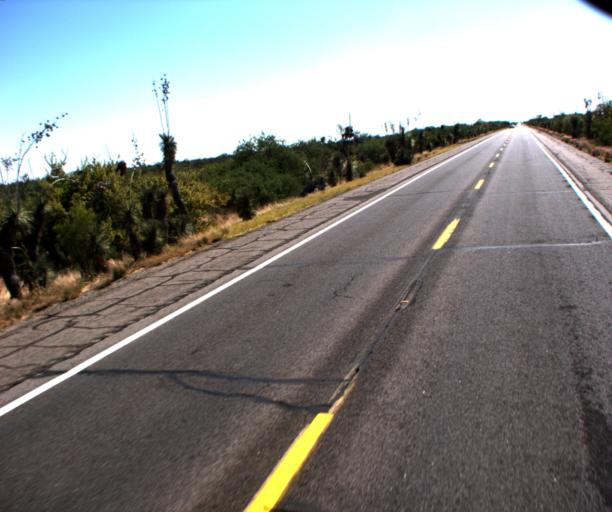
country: US
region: Arizona
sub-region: Pinal County
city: Oracle
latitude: 32.6153
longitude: -110.8263
